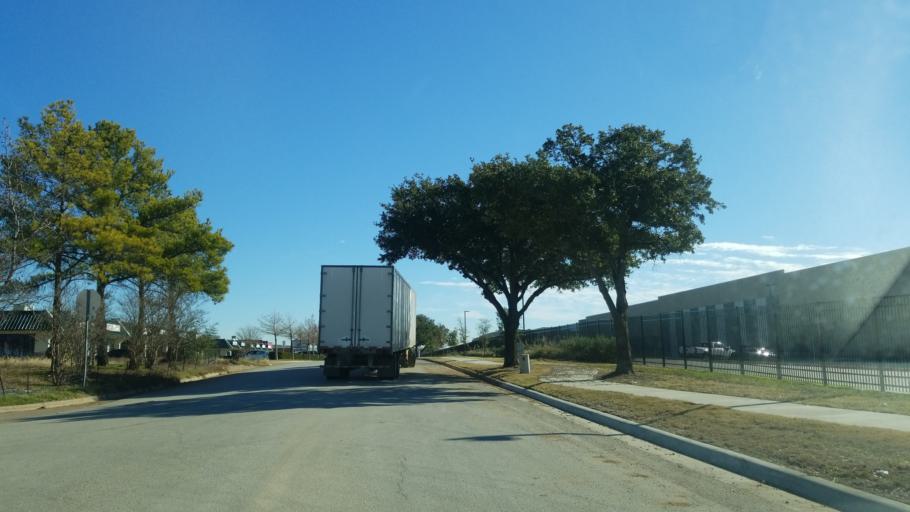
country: US
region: Texas
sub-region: Tarrant County
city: Arlington
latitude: 32.7464
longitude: -97.0600
